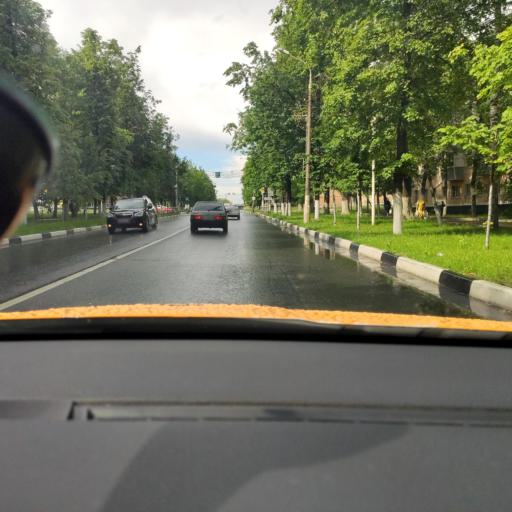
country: RU
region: Moskovskaya
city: Stupino
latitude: 54.8958
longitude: 38.0800
